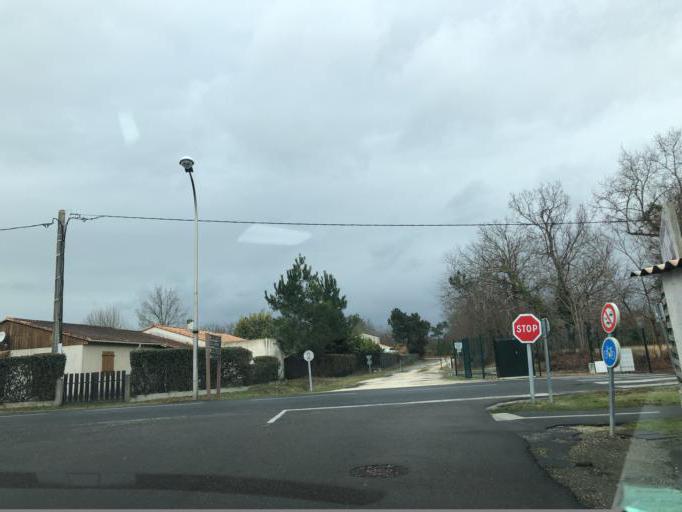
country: FR
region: Aquitaine
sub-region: Departement de la Gironde
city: Hourtin
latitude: 45.1820
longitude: -1.0759
